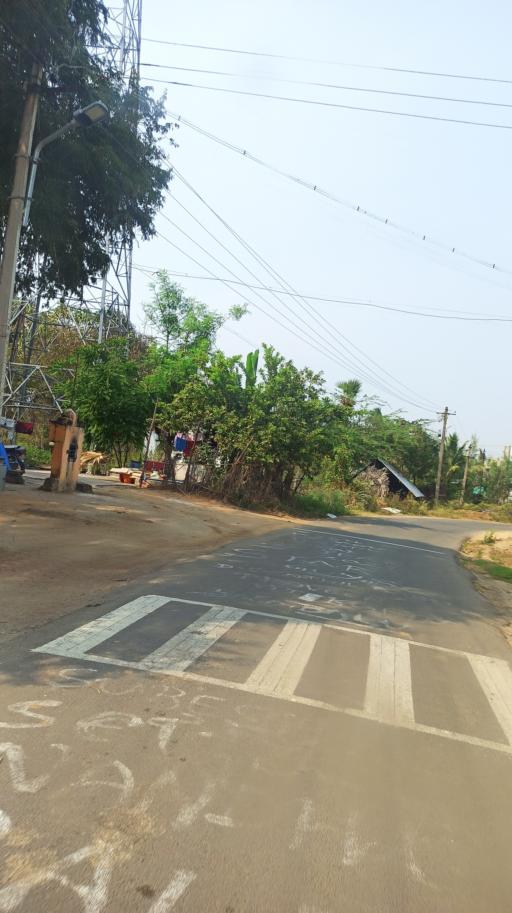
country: IN
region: Tamil Nadu
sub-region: Tiruvannamalai
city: Desur
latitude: 12.4401
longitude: 79.3899
